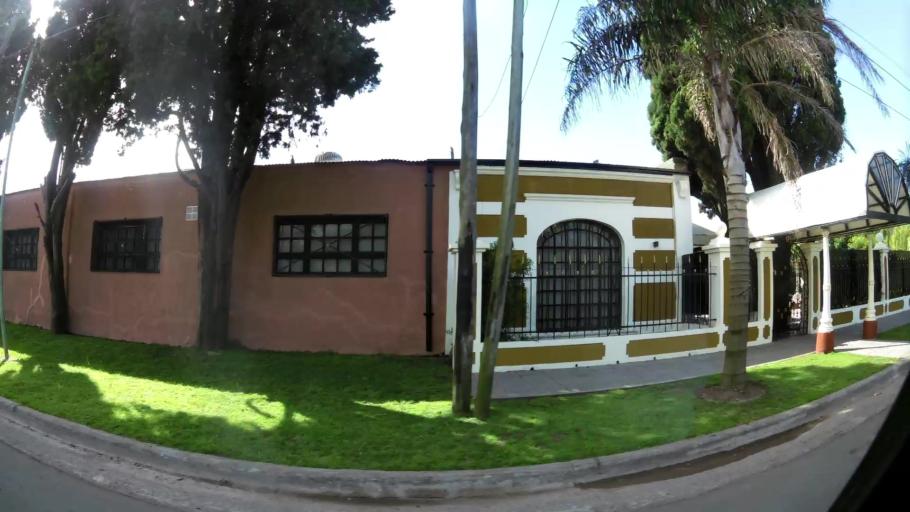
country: AR
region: Buenos Aires
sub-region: Partido de Almirante Brown
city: Adrogue
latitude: -34.8005
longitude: -58.3531
